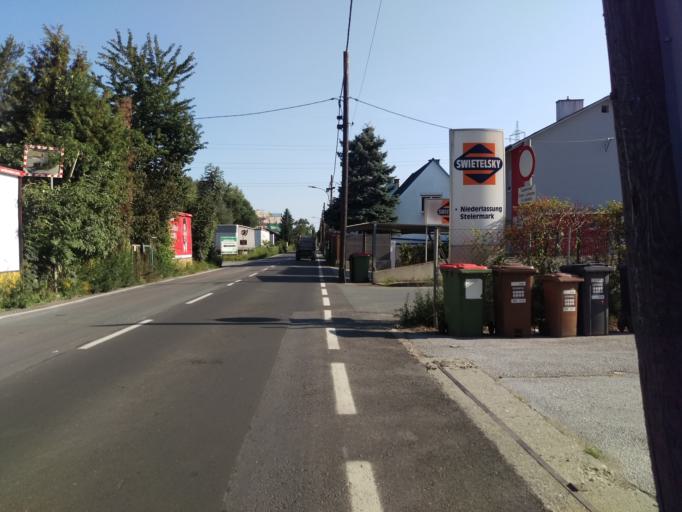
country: AT
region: Styria
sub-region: Politischer Bezirk Graz-Umgebung
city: Feldkirchen bei Graz
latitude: 47.0367
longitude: 15.4399
